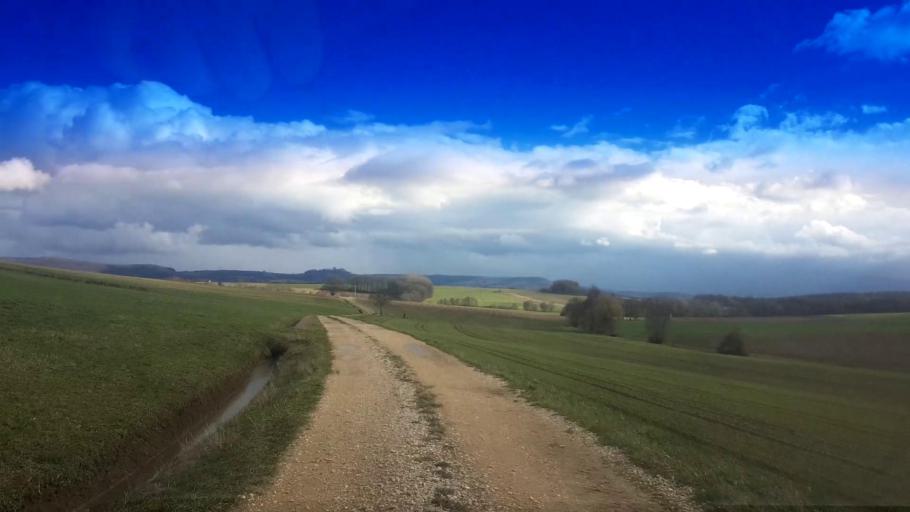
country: DE
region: Bavaria
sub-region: Upper Franconia
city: Schesslitz
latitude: 49.9967
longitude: 11.0136
